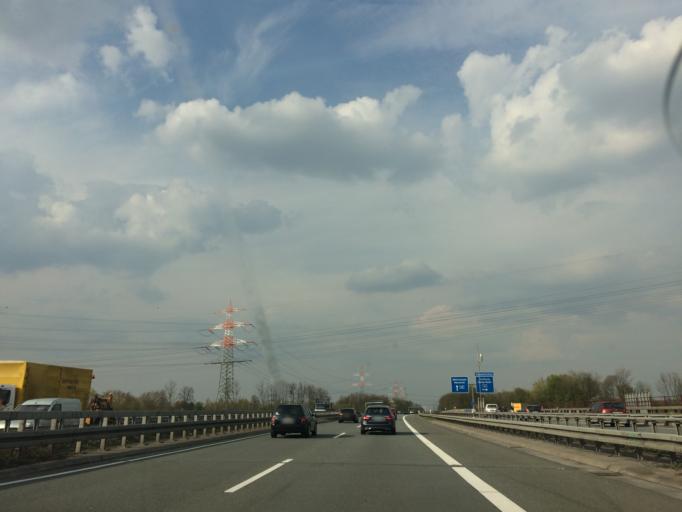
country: DE
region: North Rhine-Westphalia
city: Castrop-Rauxel
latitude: 51.5609
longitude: 7.3580
